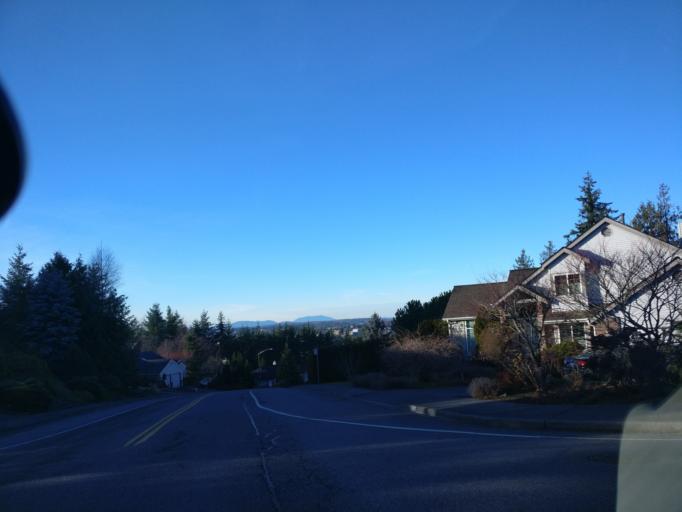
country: US
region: Washington
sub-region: Skagit County
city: Mount Vernon
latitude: 48.4263
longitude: -122.2902
